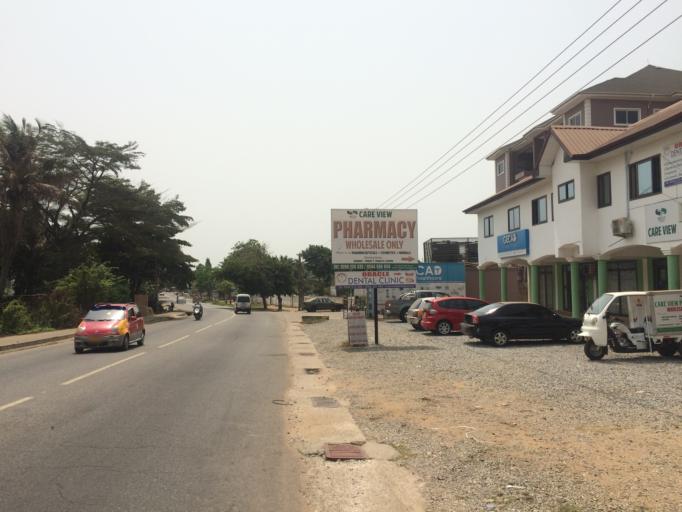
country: GH
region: Greater Accra
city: Accra
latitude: 5.5450
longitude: -0.2401
